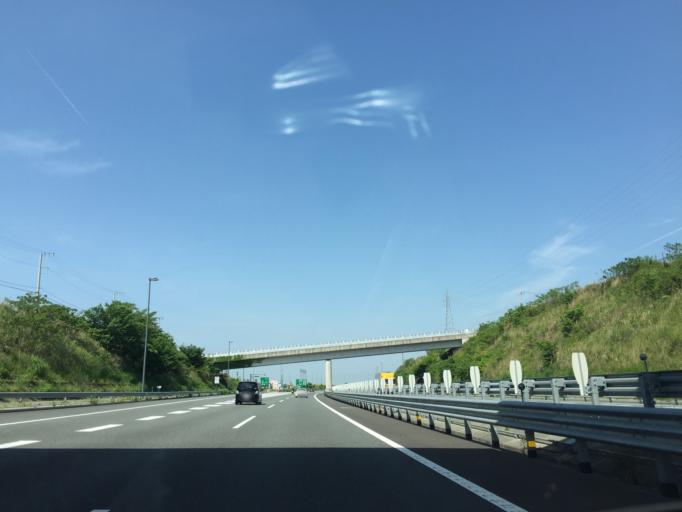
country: JP
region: Shizuoka
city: Numazu
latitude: 35.1536
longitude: 138.8160
